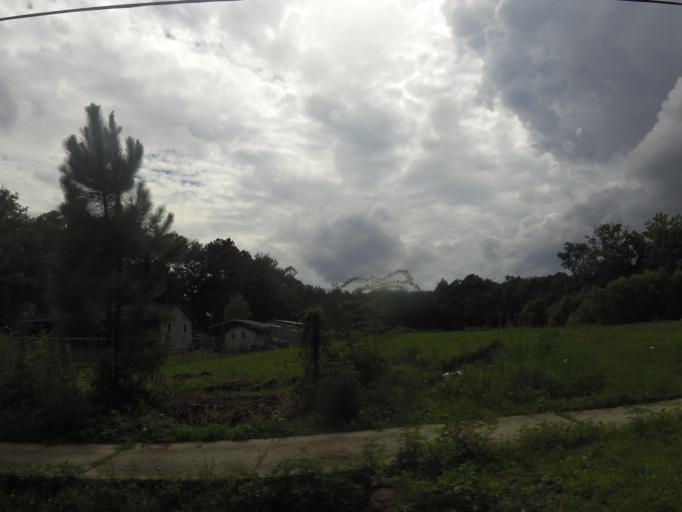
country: US
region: Florida
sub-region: Duval County
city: Jacksonville
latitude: 30.3020
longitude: -81.5308
